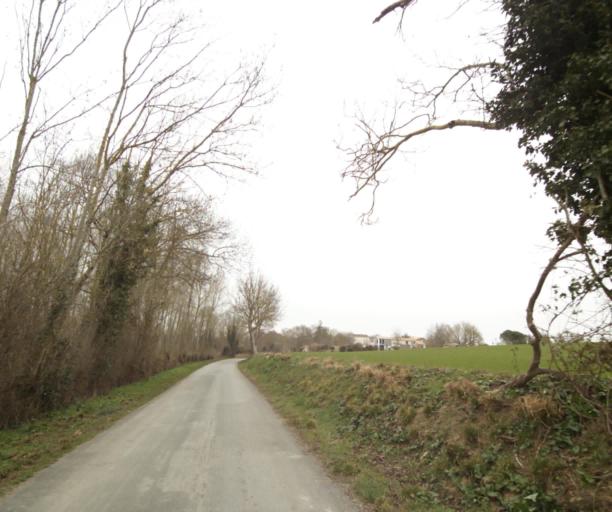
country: FR
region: Poitou-Charentes
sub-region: Departement des Deux-Sevres
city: Magne
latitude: 46.3212
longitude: -0.5327
